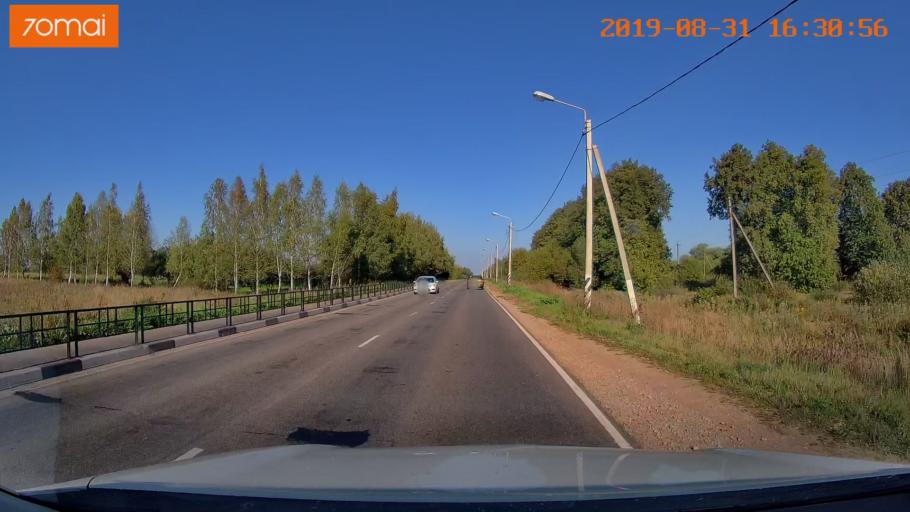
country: RU
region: Kaluga
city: Babynino
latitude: 54.5132
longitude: 35.8428
